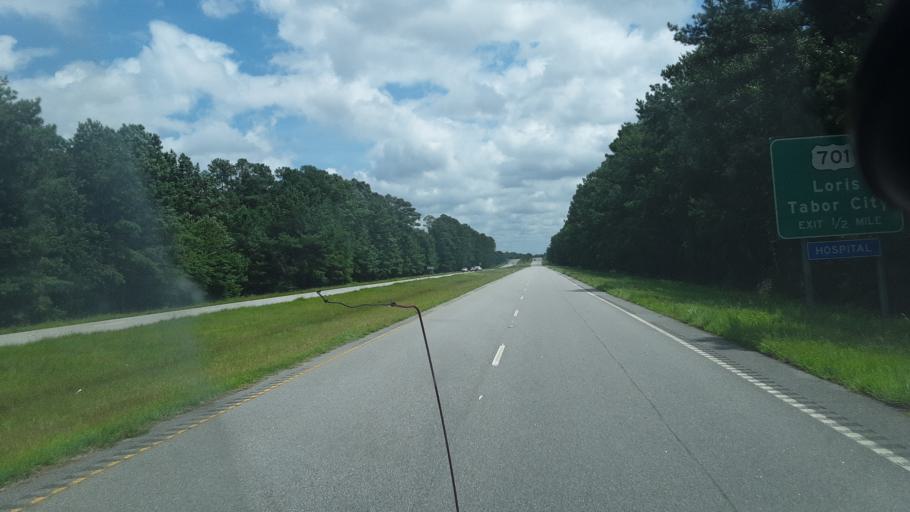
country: US
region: South Carolina
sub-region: Horry County
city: Loris
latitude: 34.0857
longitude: -78.8847
